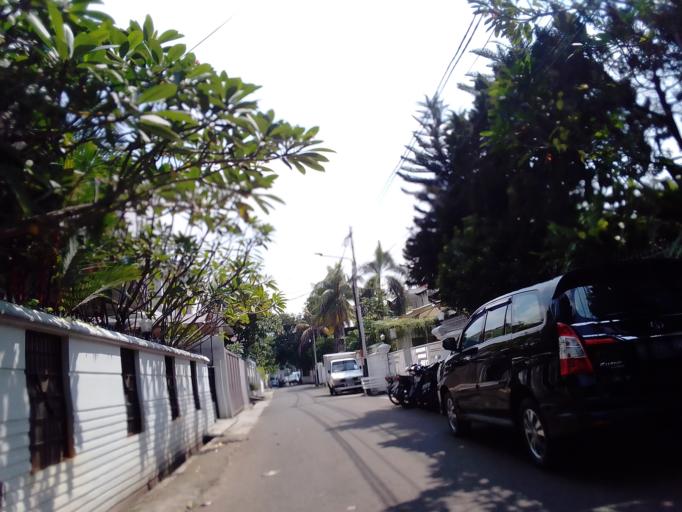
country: ID
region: Jakarta Raya
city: Jakarta
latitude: -6.2569
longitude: 106.8042
